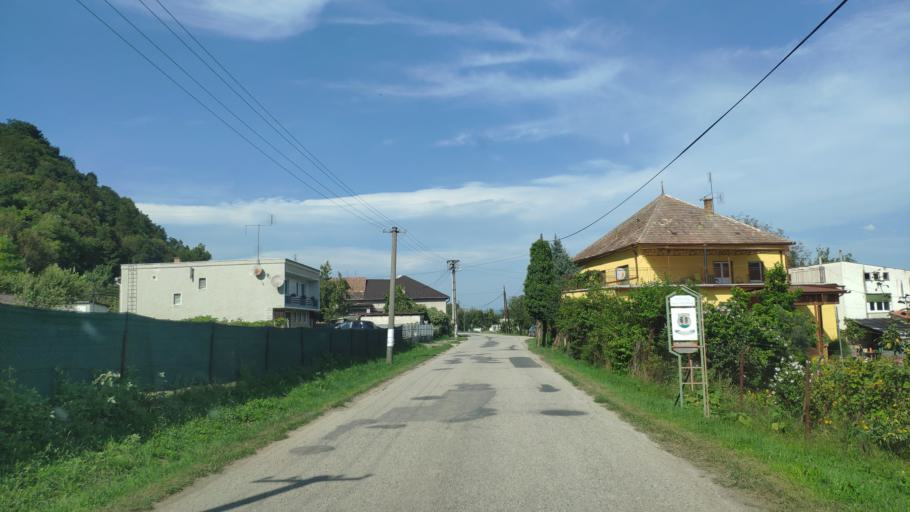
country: HU
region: Borsod-Abauj-Zemplen
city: Putnok
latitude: 48.4412
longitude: 20.3142
